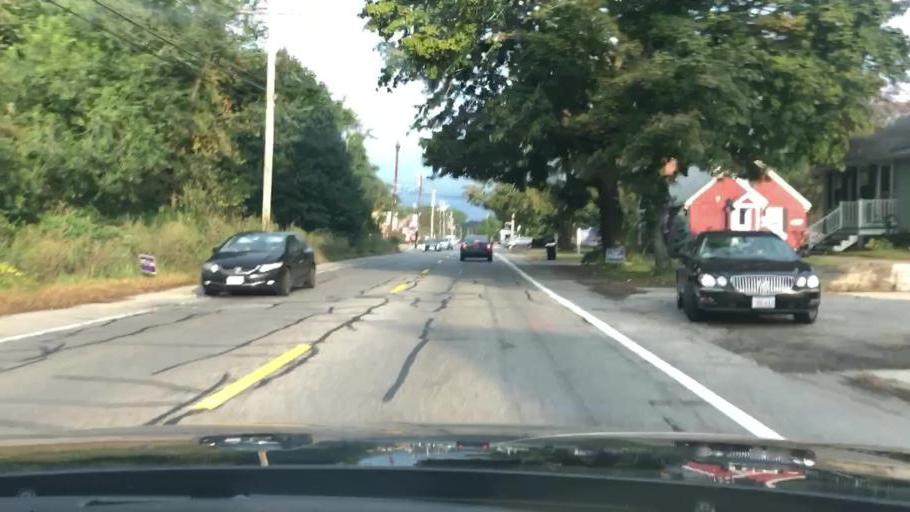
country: US
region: Massachusetts
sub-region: Middlesex County
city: Tyngsboro
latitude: 42.6438
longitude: -71.3902
